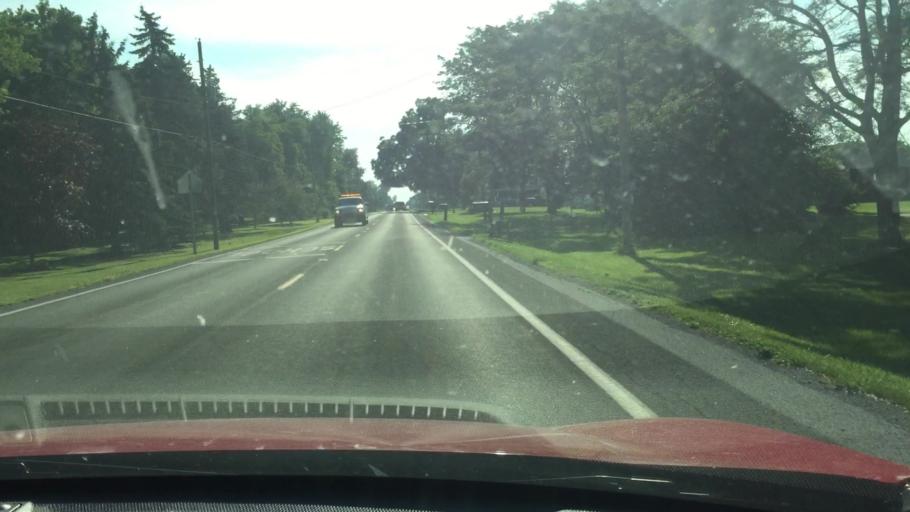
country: US
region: Ohio
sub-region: Hardin County
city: Ada
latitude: 40.7766
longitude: -83.8384
